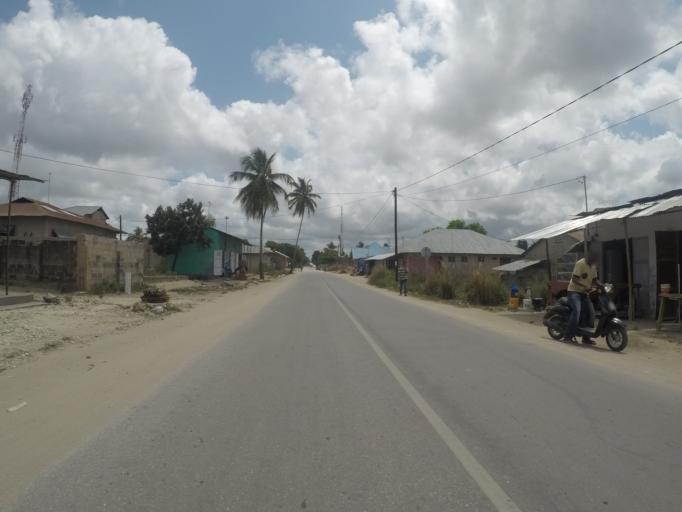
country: TZ
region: Zanzibar Urban/West
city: Zanzibar
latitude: -6.1985
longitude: 39.2438
